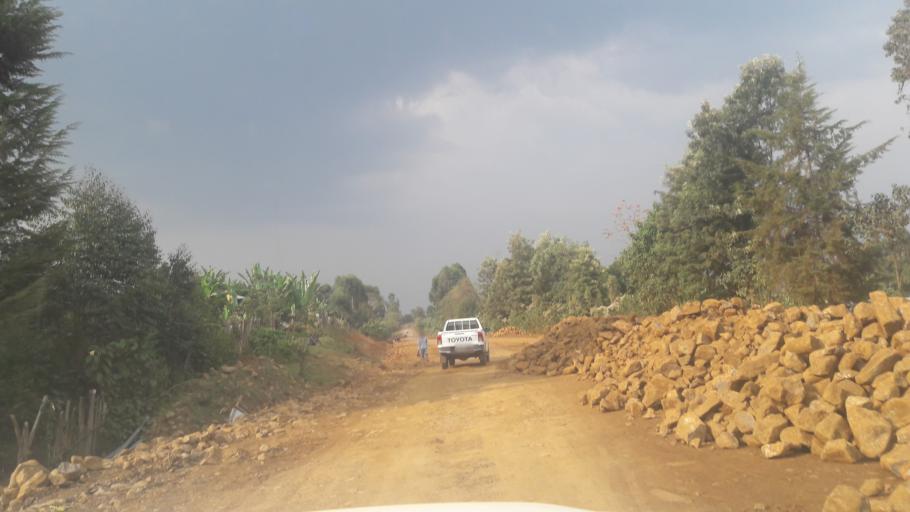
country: ET
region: Oromiya
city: Gore
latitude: 7.7228
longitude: 35.4831
